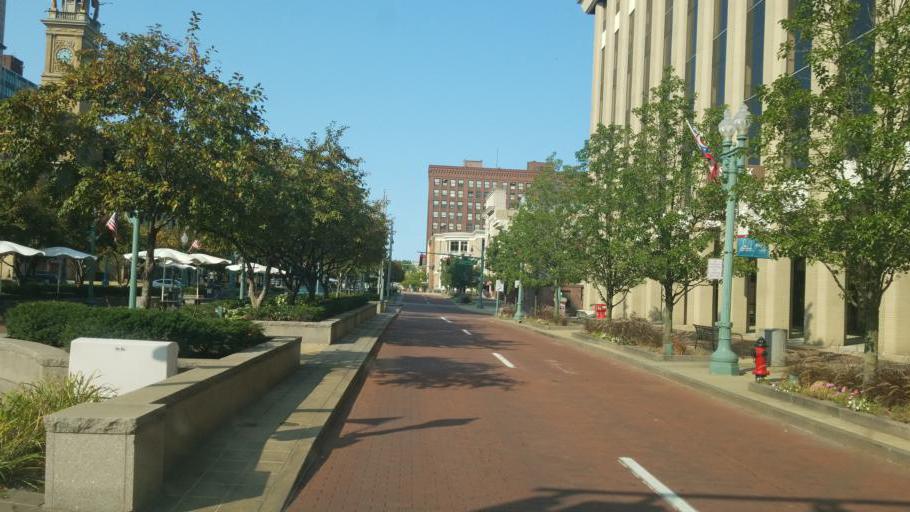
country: US
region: Ohio
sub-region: Stark County
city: Canton
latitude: 40.7978
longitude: -81.3748
